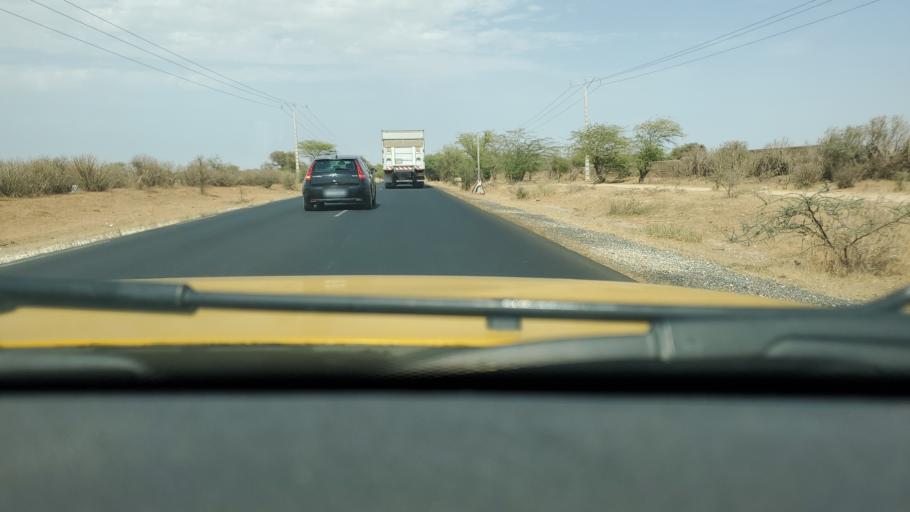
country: SN
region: Saint-Louis
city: Saint-Louis
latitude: 15.9309
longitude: -16.3375
